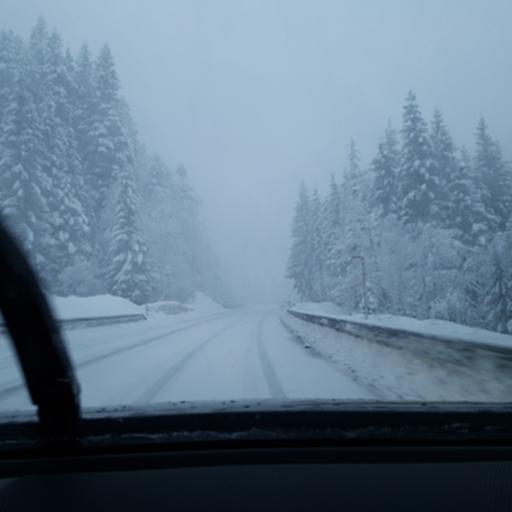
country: AT
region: Upper Austria
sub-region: Politischer Bezirk Gmunden
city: Bad Goisern
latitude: 47.5898
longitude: 13.5100
